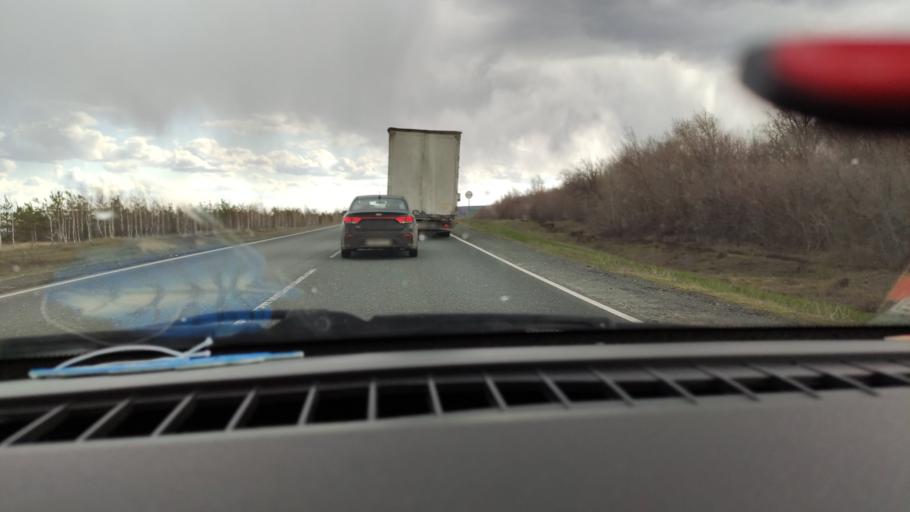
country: RU
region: Saratov
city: Balakovo
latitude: 52.1600
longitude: 47.8208
